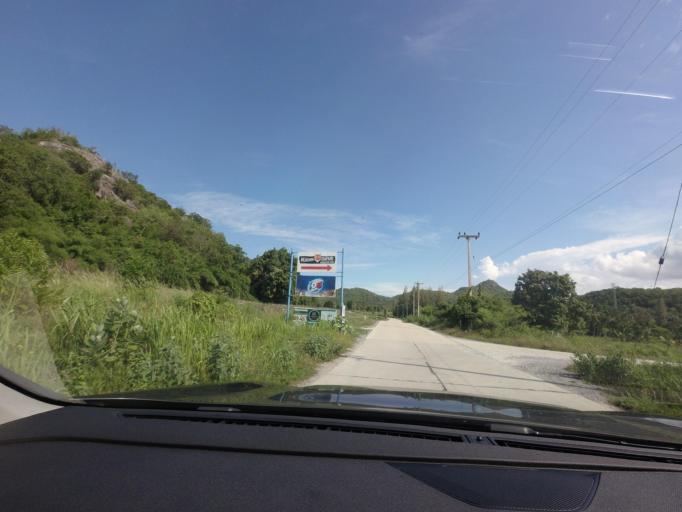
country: TH
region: Prachuap Khiri Khan
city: Hua Hin
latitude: 12.4761
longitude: 99.9367
